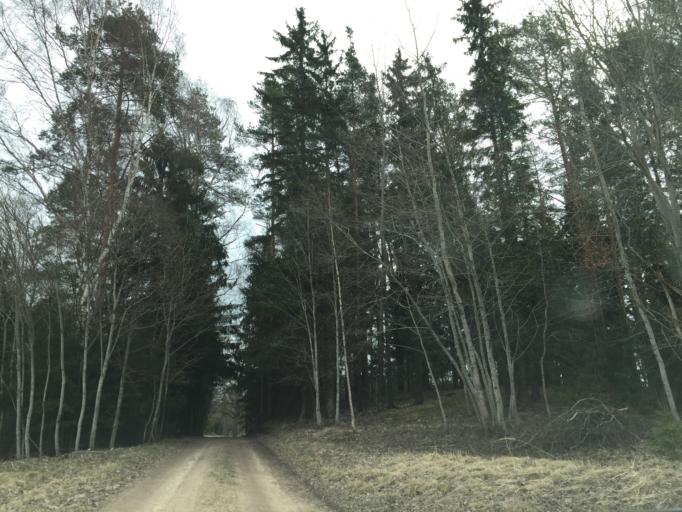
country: LV
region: Priekuli
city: Priekuli
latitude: 57.2918
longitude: 25.3261
